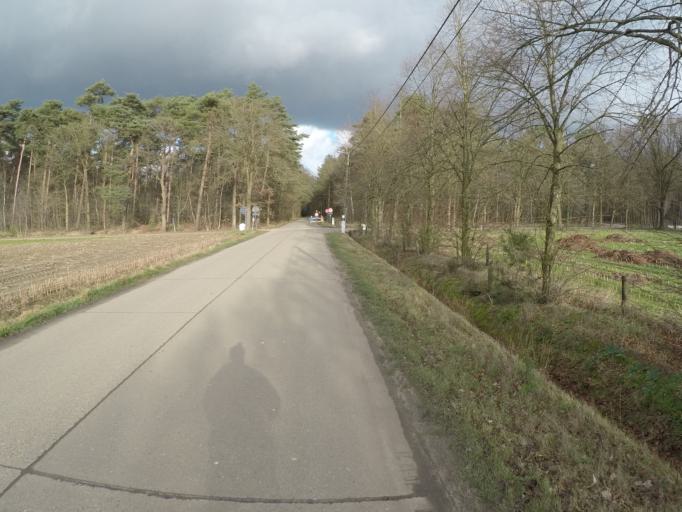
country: BE
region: Flanders
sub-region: Provincie Antwerpen
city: Lille
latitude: 51.2531
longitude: 4.7767
